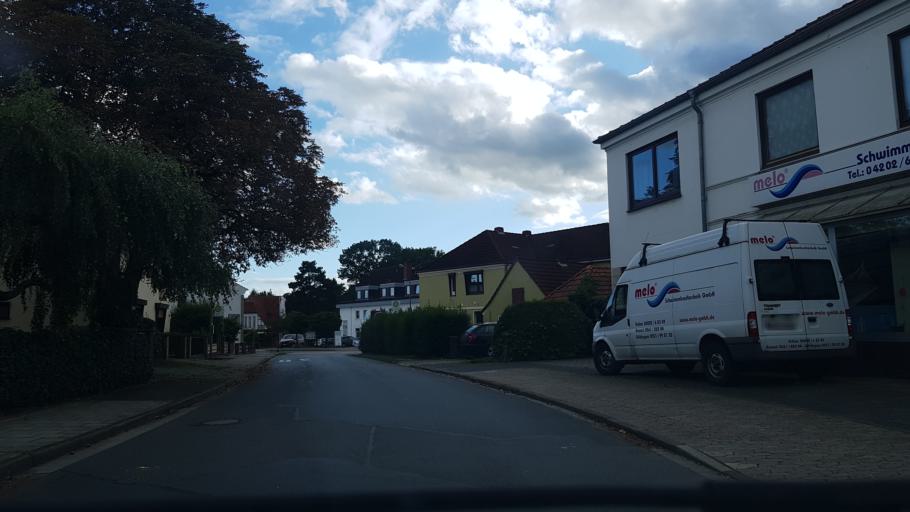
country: DE
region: Lower Saxony
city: Oyten
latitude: 53.0295
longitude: 8.9713
